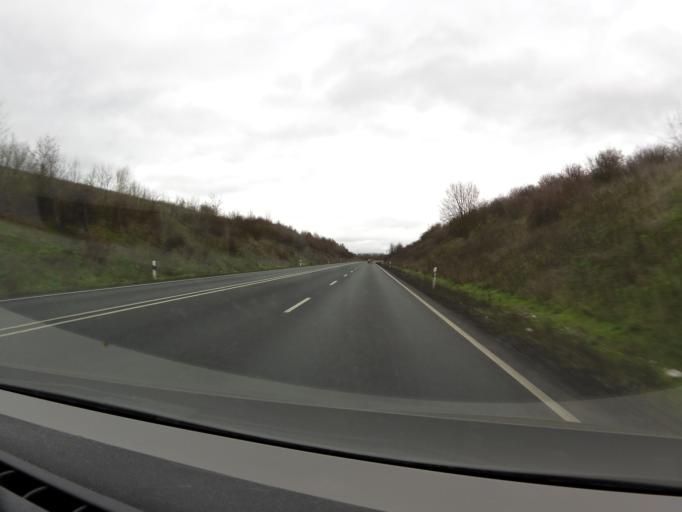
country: DE
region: Saxony-Anhalt
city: Oberroblingen
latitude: 51.4564
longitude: 11.3082
